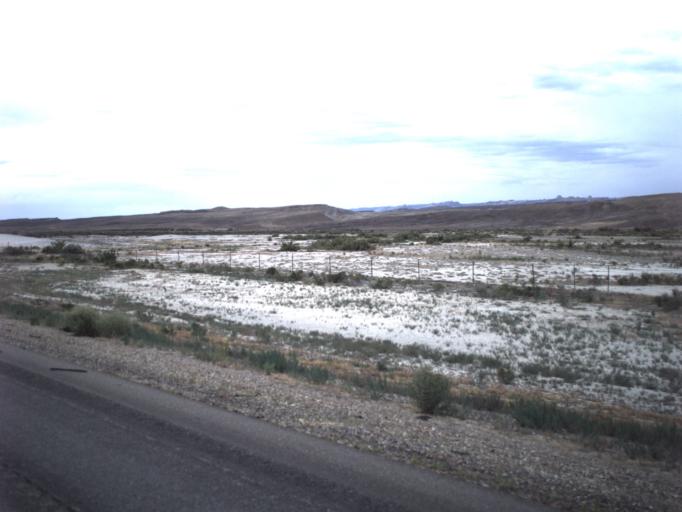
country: US
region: Utah
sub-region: Carbon County
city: East Carbon City
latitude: 39.1098
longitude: -110.3266
